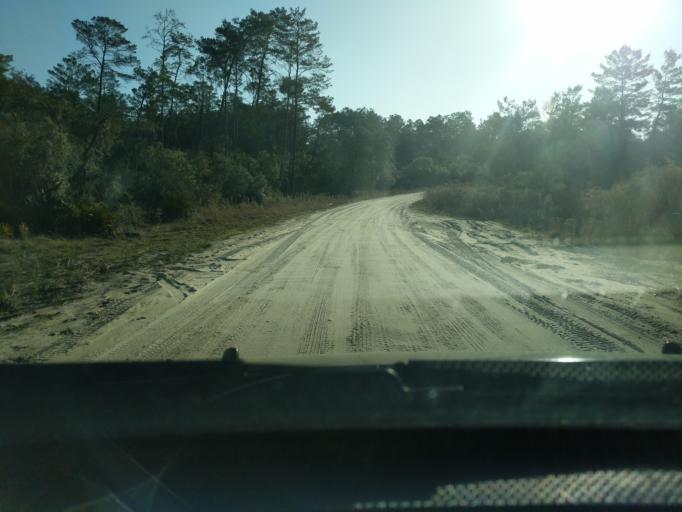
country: US
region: Florida
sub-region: Marion County
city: Silver Springs Shores
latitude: 29.2180
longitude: -81.8260
